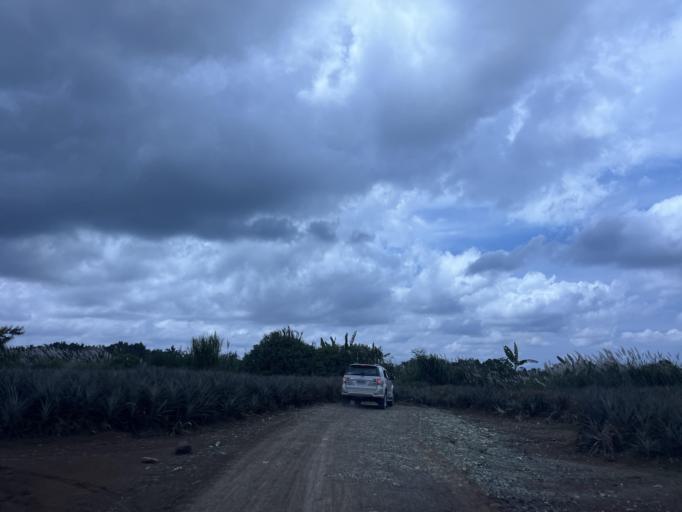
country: PH
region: Northern Mindanao
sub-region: Province of Bukidnon
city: Sumilao
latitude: 8.2986
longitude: 124.9298
